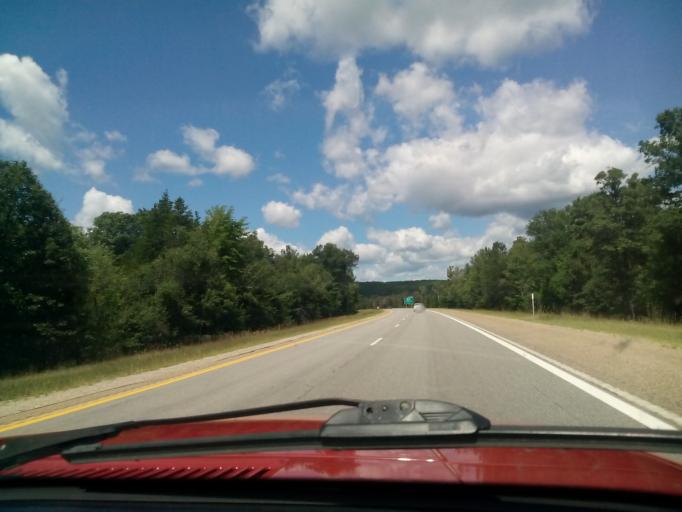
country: US
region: Michigan
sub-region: Roscommon County
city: Roscommon
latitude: 44.4373
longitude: -84.5952
